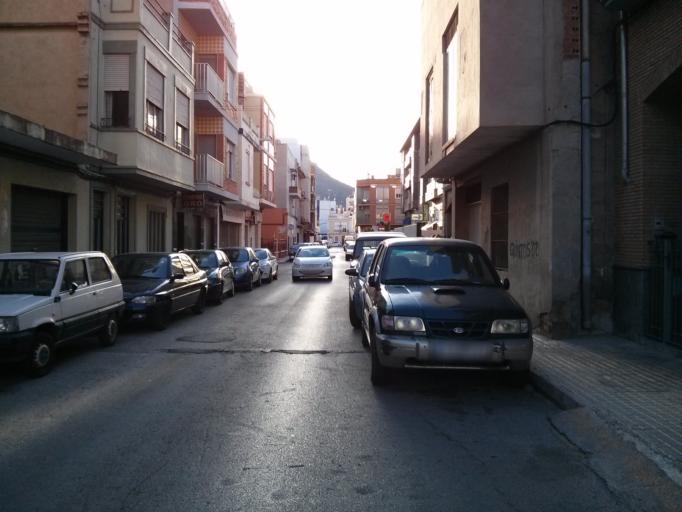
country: ES
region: Valencia
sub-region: Provincia de Castello
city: Alfondeguilla
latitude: 39.8226
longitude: -0.2309
